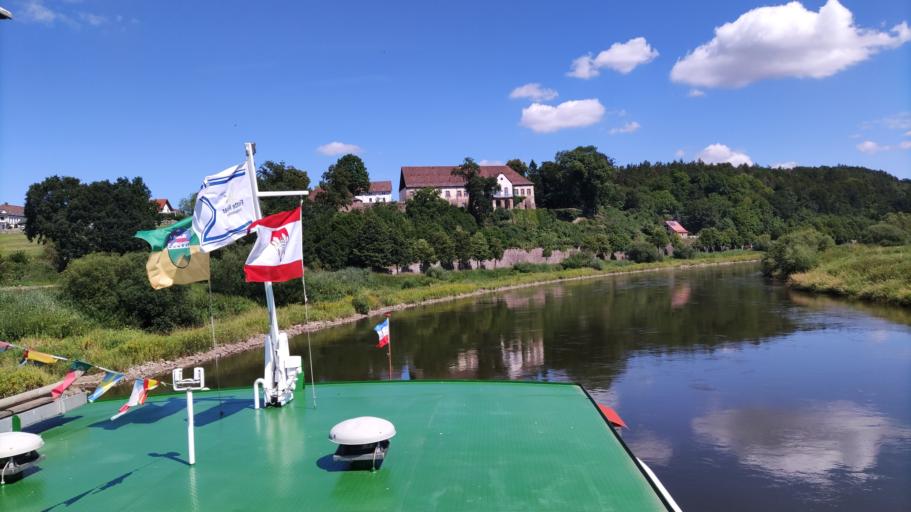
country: DE
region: North Rhine-Westphalia
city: Beverungen
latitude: 51.6896
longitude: 9.3883
